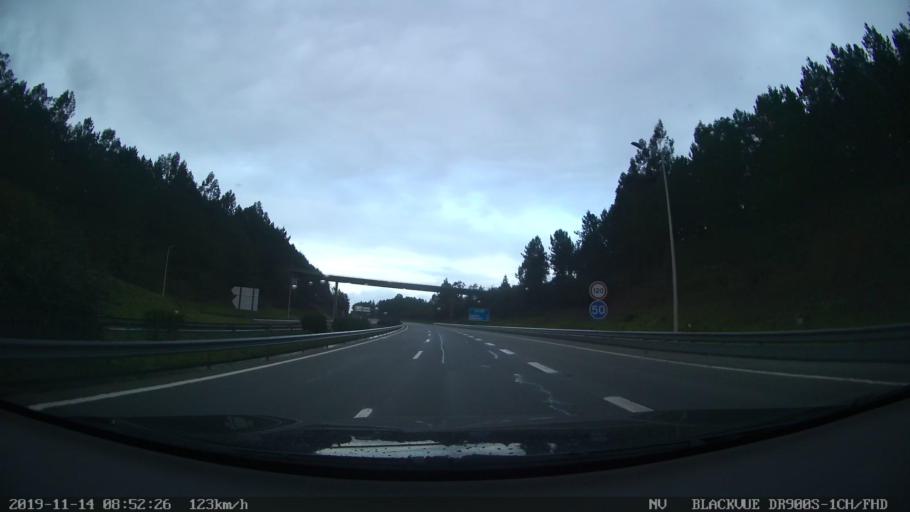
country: PT
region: Viana do Castelo
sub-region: Vila Nova de Cerveira
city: Vila Nova de Cerveira
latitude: 41.9274
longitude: -8.6525
